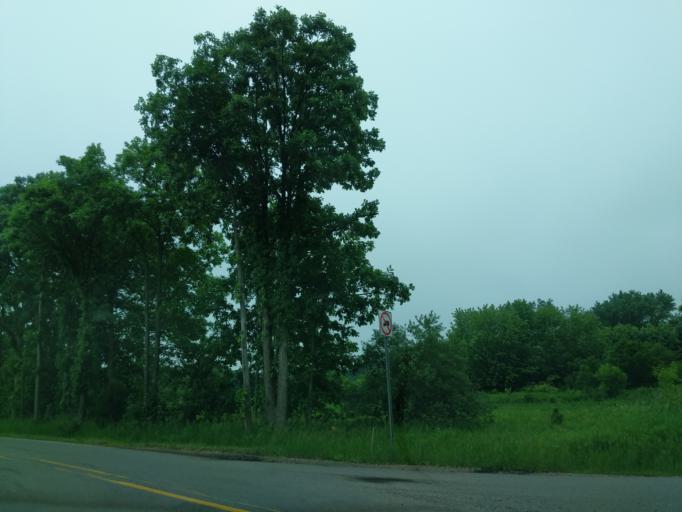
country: US
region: Michigan
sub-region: Jackson County
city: Spring Arbor
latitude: 42.2183
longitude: -84.5704
